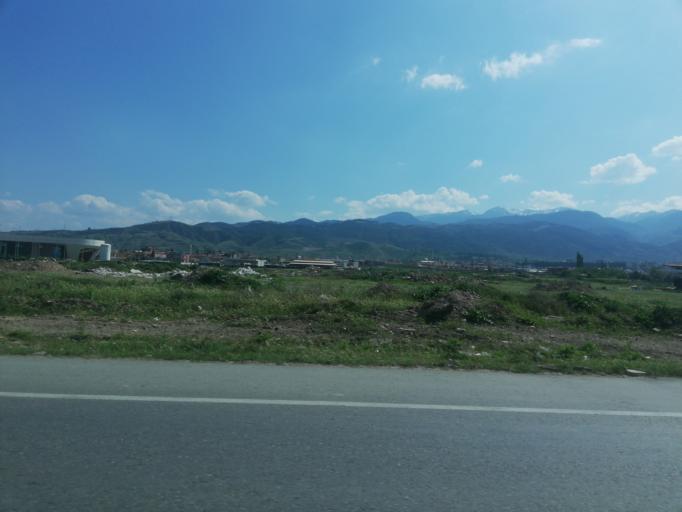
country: TR
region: Manisa
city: Alasehir
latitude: 38.3592
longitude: 28.5370
